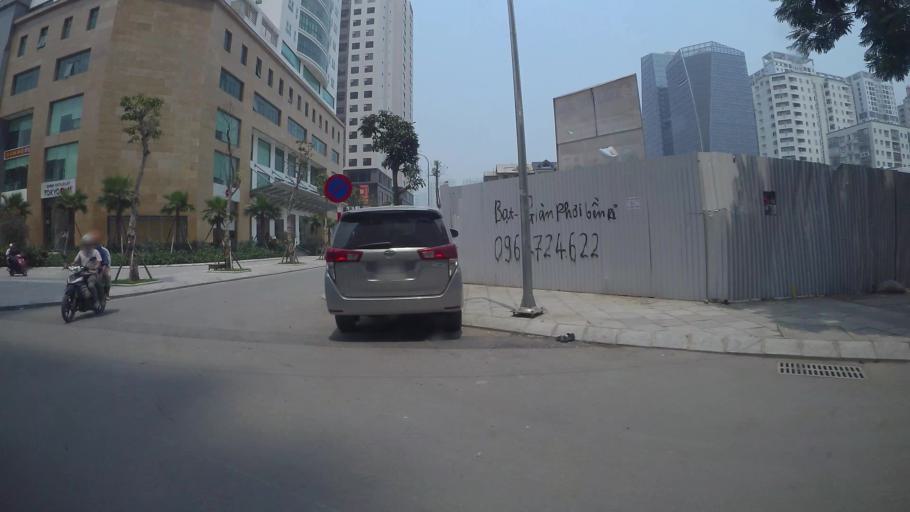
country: VN
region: Ha Noi
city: Thanh Xuan
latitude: 20.9995
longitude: 105.8014
